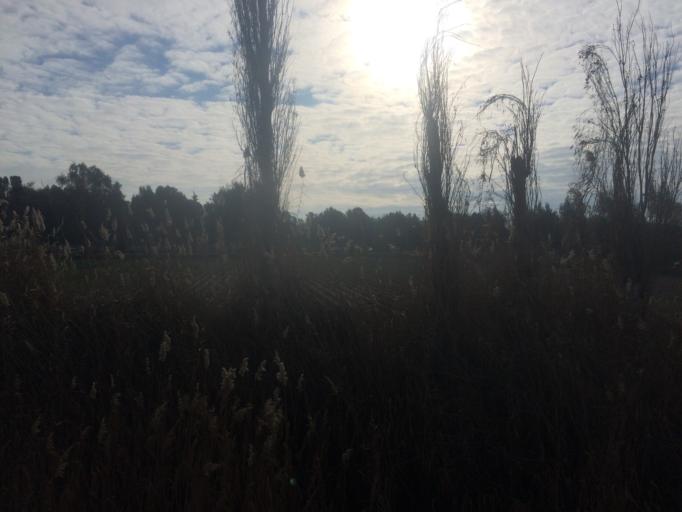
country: TR
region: Izmir
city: Karsiyaka
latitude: 38.4937
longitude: 26.9589
